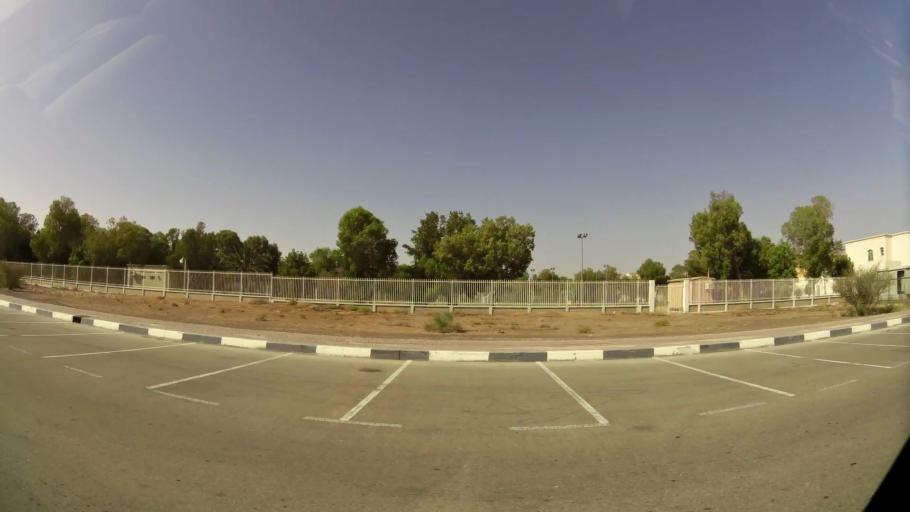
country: OM
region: Al Buraimi
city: Al Buraymi
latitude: 24.3383
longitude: 55.8016
